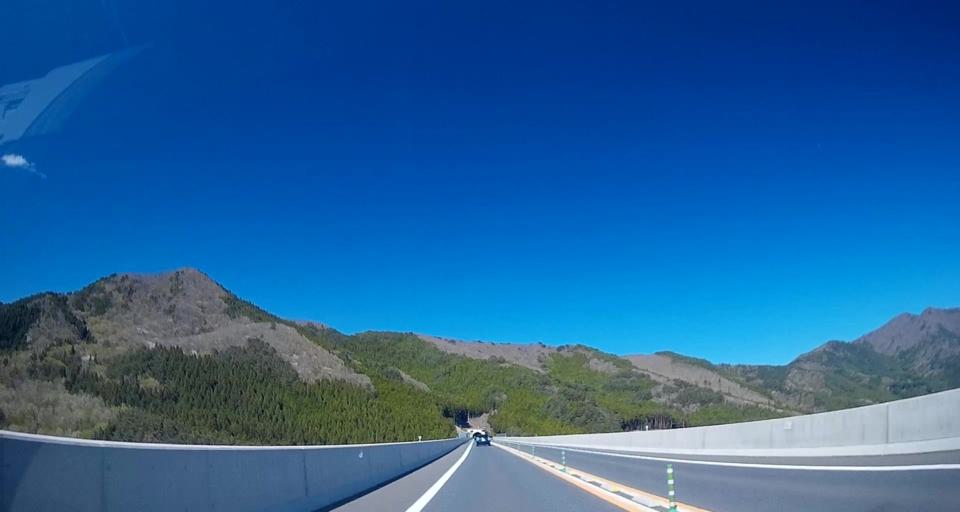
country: JP
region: Iwate
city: Ofunato
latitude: 39.1275
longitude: 141.8009
